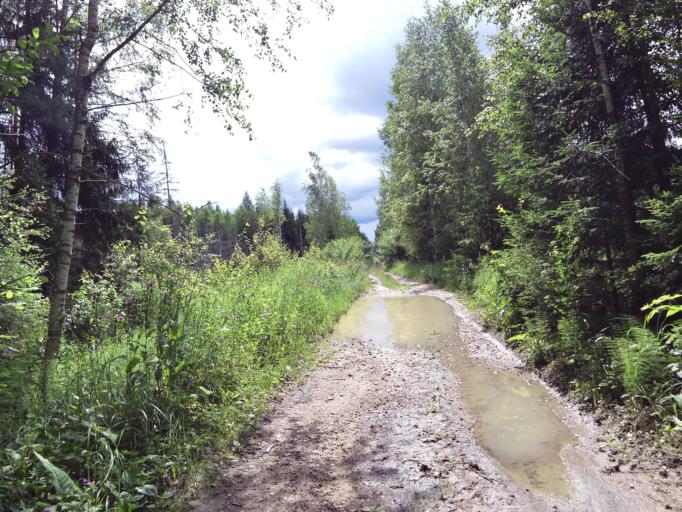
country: RU
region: Moskovskaya
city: Popovo
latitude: 54.9758
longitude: 37.6953
